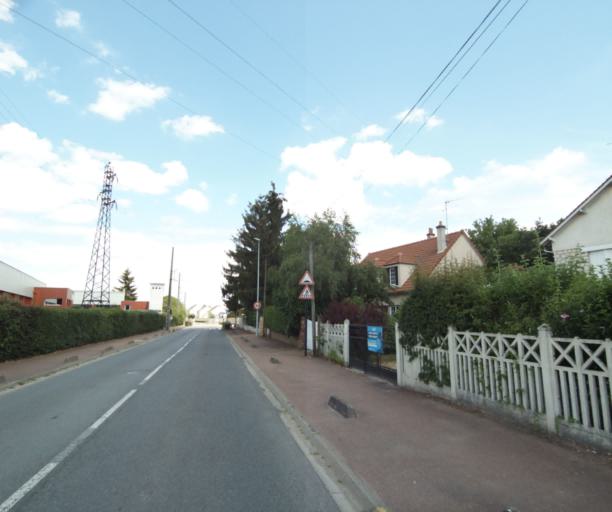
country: FR
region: Ile-de-France
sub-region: Departement de Seine-et-Marne
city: Samoreau
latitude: 48.4356
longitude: 2.7538
